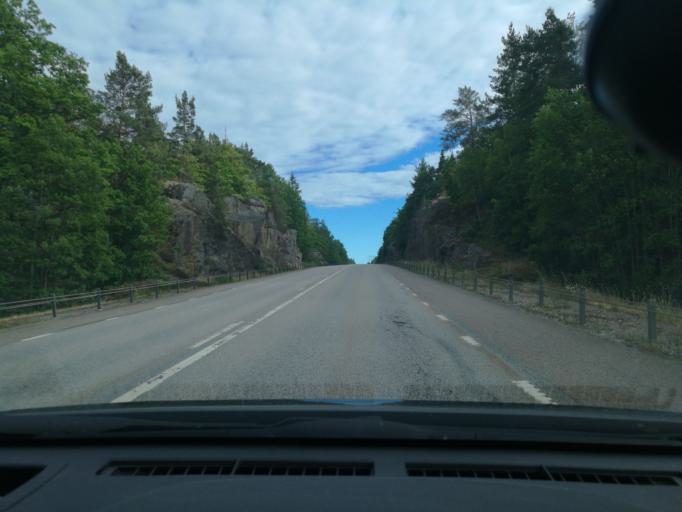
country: SE
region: Kalmar
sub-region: Vasterviks Kommun
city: Ankarsrum
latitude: 57.5447
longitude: 16.4791
